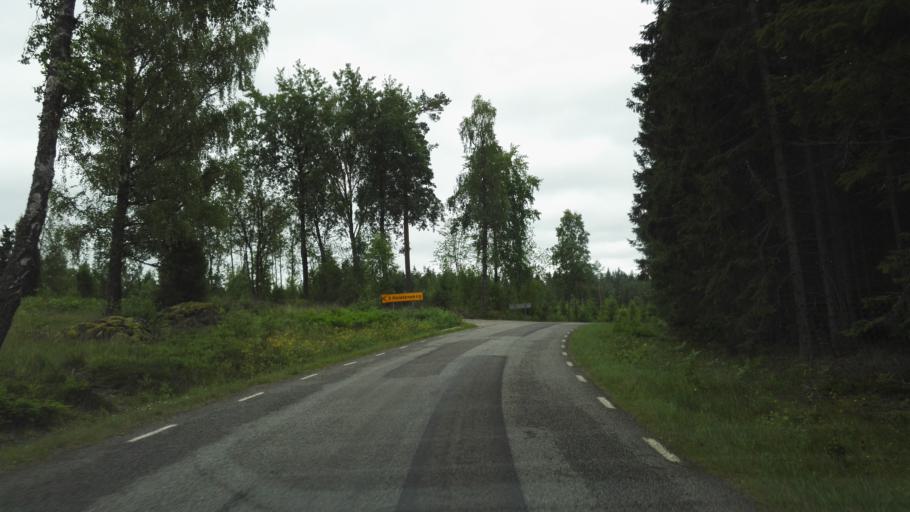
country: SE
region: Kronoberg
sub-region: Vaxjo Kommun
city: Rottne
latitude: 57.1222
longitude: 14.8139
